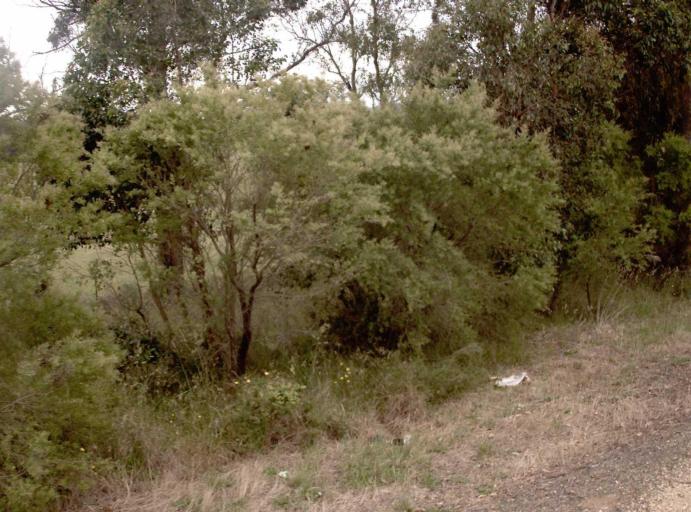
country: AU
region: Victoria
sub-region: East Gippsland
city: Bairnsdale
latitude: -37.7803
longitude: 147.5973
